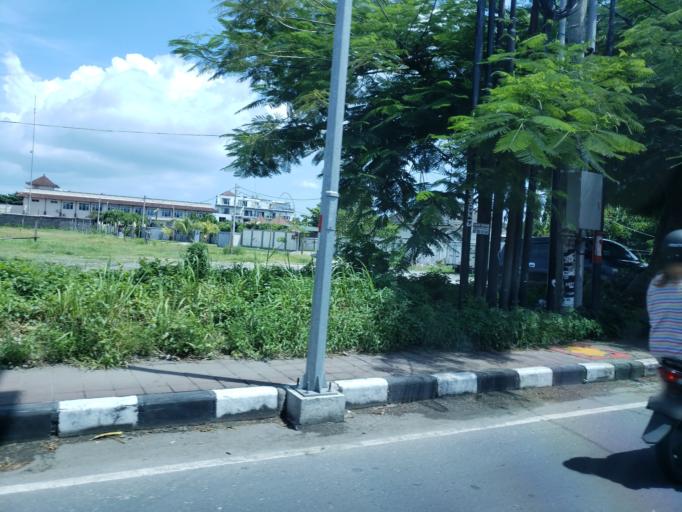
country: ID
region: Bali
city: Kelanabian
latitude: -8.7555
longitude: 115.1773
